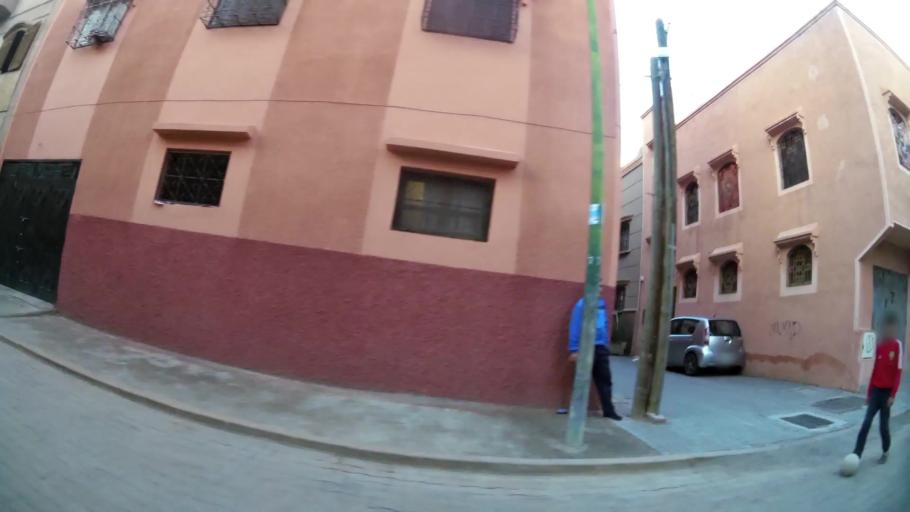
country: MA
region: Marrakech-Tensift-Al Haouz
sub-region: Marrakech
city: Marrakesh
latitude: 31.6371
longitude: -8.0374
